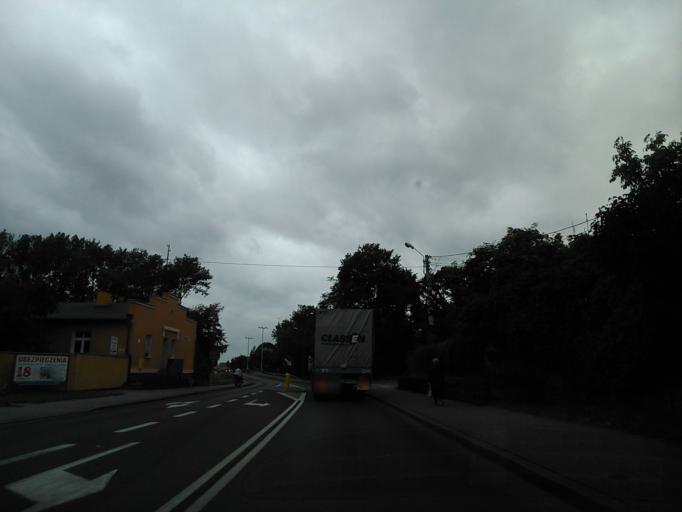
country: PL
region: Kujawsko-Pomorskie
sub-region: Powiat inowroclawski
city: Kruszwica
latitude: 52.6743
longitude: 18.3314
